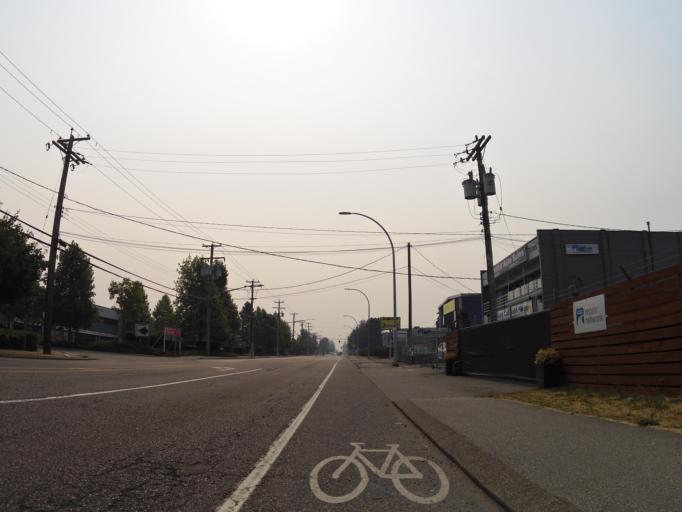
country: CA
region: British Columbia
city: Surrey
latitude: 49.1448
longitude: -122.8568
